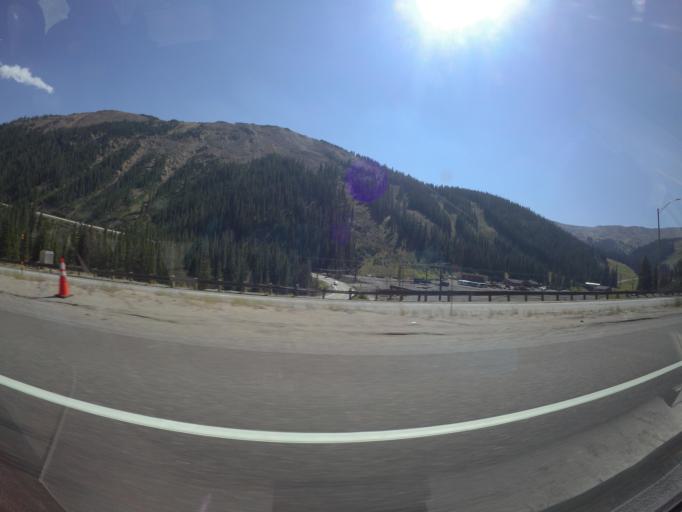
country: US
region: Colorado
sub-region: Summit County
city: Keystone
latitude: 39.6823
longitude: -105.8953
